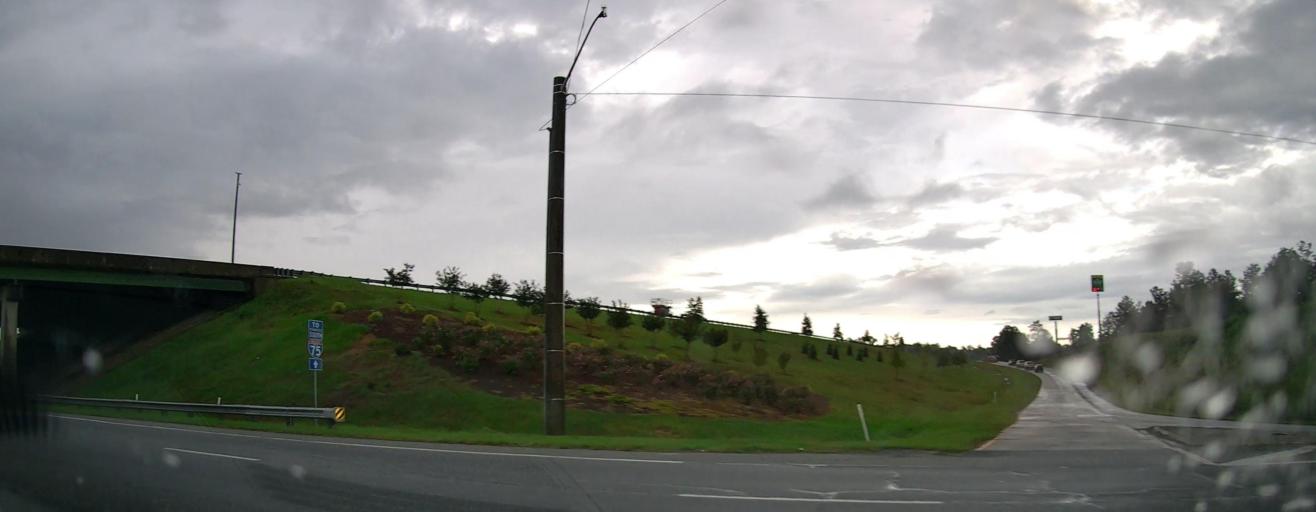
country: US
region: Georgia
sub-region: Bibb County
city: West Point
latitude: 32.8113
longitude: -83.7195
